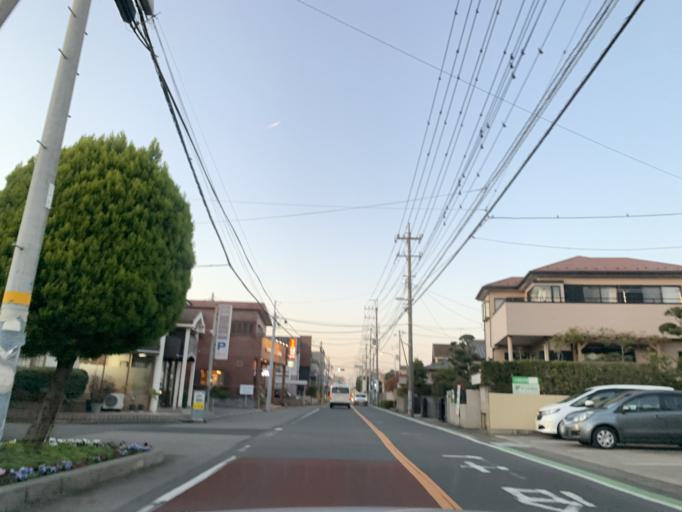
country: JP
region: Chiba
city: Nagareyama
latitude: 35.9009
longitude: 139.9069
